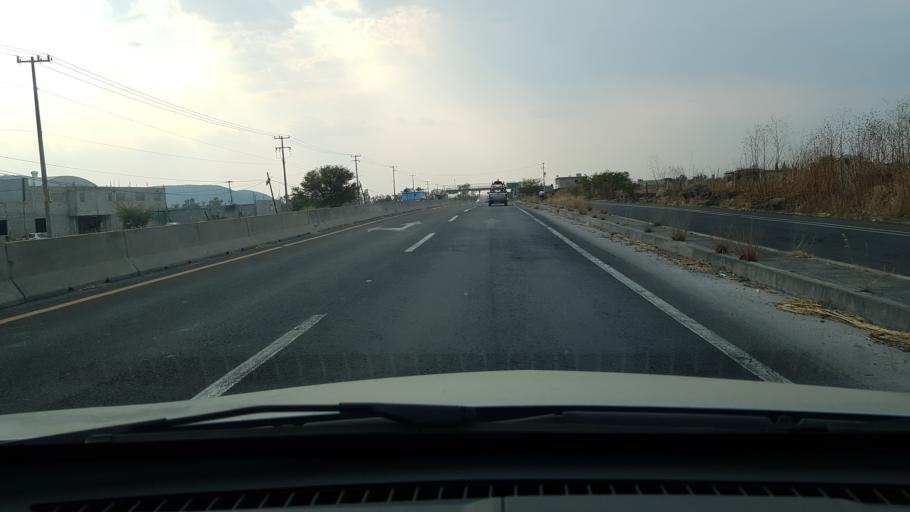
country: MX
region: Morelos
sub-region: Ayala
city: Unidad Habitacional Mariano Matamoros
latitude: 18.7421
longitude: -98.8340
